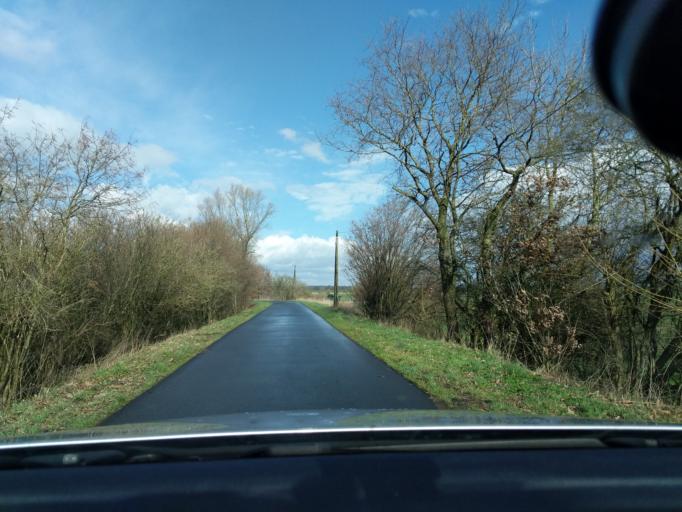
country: DE
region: Lower Saxony
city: Kranenburg
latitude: 53.6128
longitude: 9.2026
